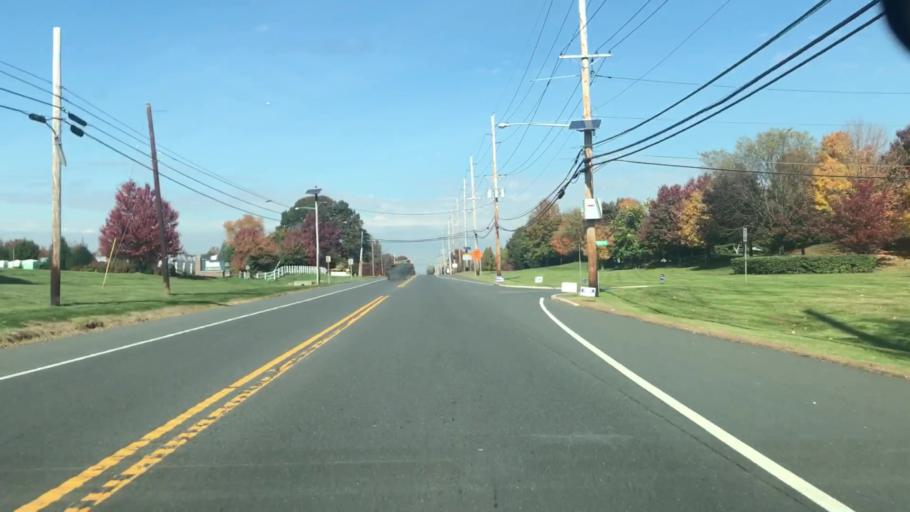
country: US
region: New Jersey
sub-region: Somerset County
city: Bloomingdale
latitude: 40.4366
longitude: -74.6610
